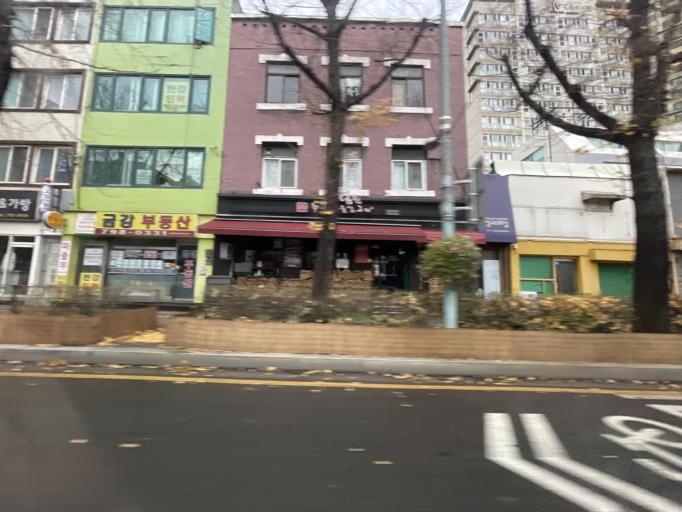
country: KR
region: Seoul
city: Seoul
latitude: 37.5310
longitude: 126.9694
